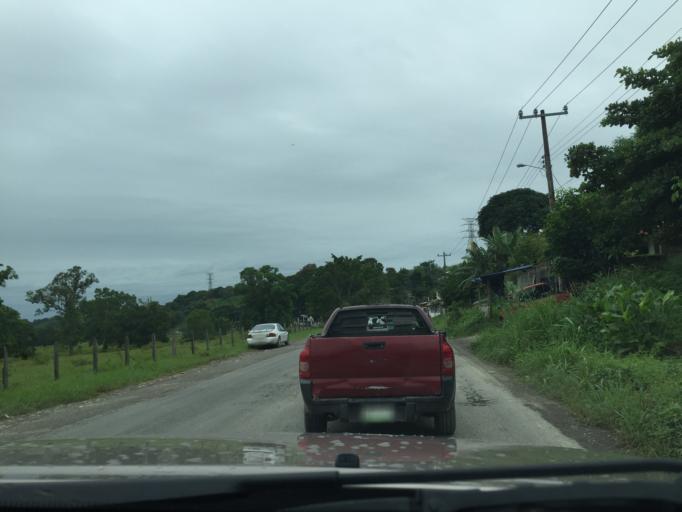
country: MX
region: Veracruz
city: Coatzintla
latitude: 20.4439
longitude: -97.4065
